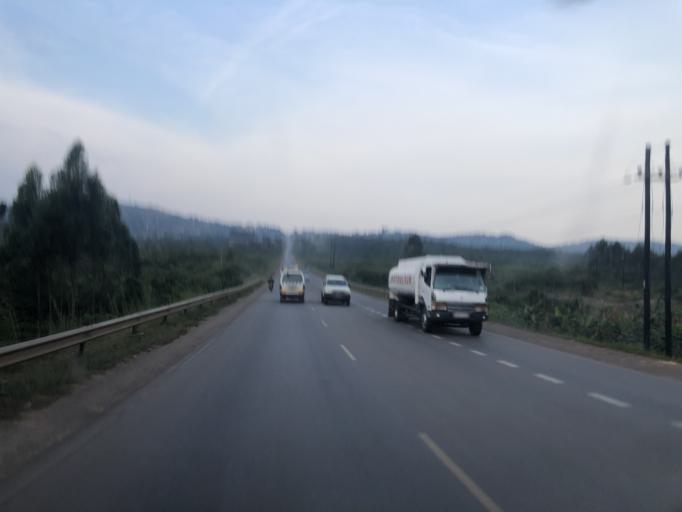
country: UG
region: Central Region
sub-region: Mpigi District
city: Mpigi
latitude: 0.2415
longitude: 32.3533
